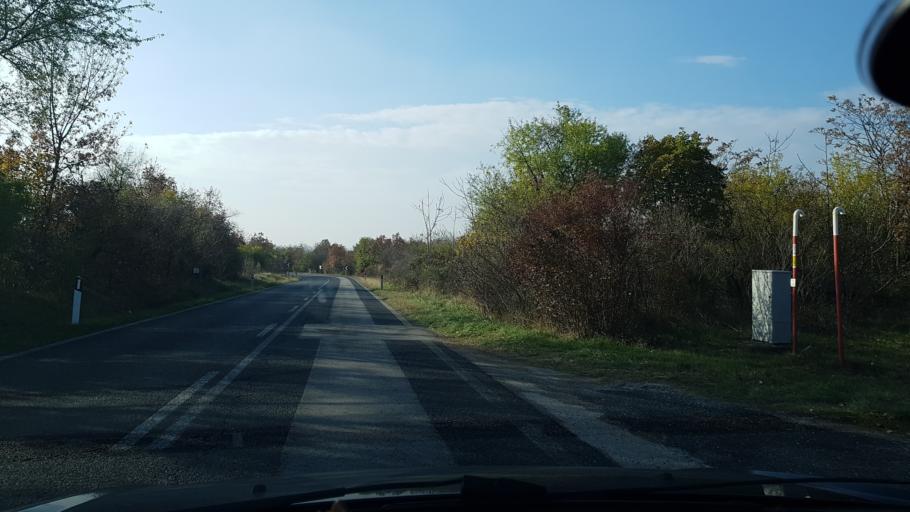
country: IT
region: Friuli Venezia Giulia
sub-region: Provincia di Gorizia
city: Ronchi dei Legionari
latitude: 45.8331
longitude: 13.5186
